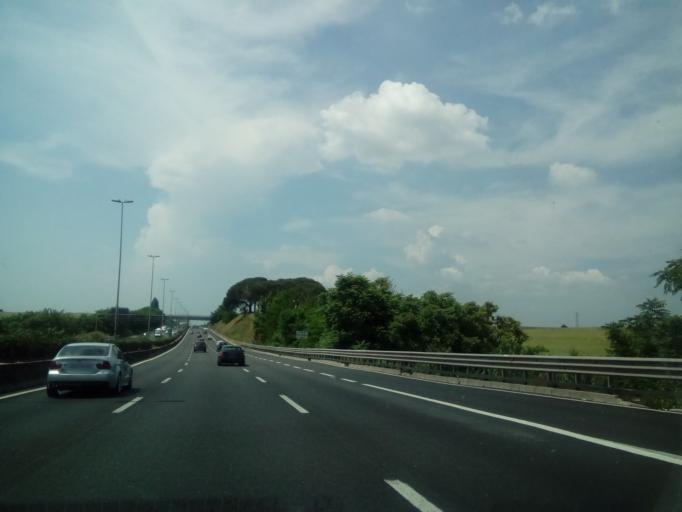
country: IT
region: Latium
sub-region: Citta metropolitana di Roma Capitale
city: Colle Verde
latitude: 41.9603
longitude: 12.5772
